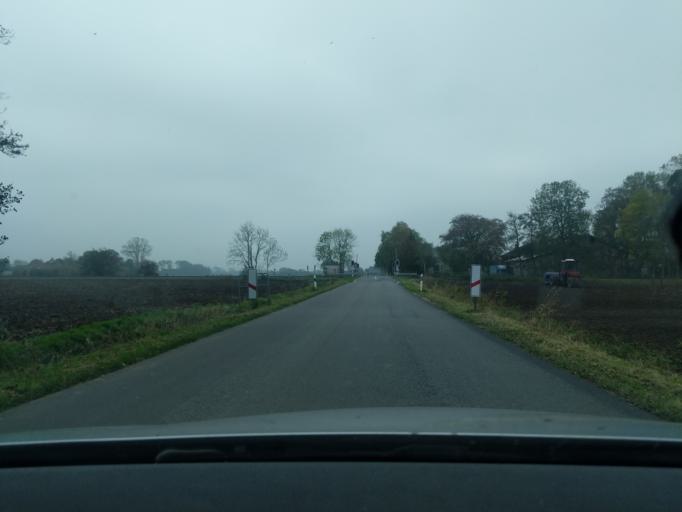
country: DE
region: Lower Saxony
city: Nordleda
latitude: 53.8263
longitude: 8.8061
